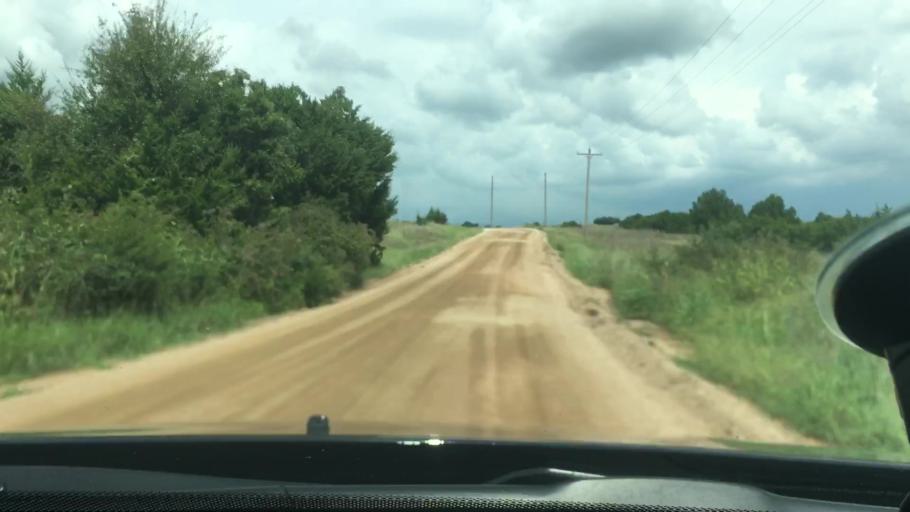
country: US
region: Oklahoma
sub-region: Carter County
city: Dickson
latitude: 34.2510
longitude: -96.9288
